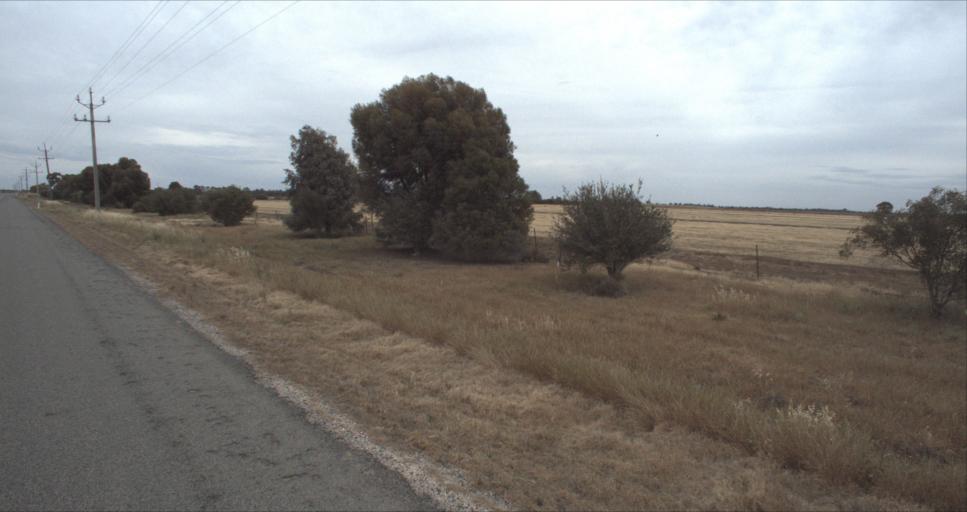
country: AU
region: New South Wales
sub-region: Leeton
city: Leeton
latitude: -34.4920
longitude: 146.4013
